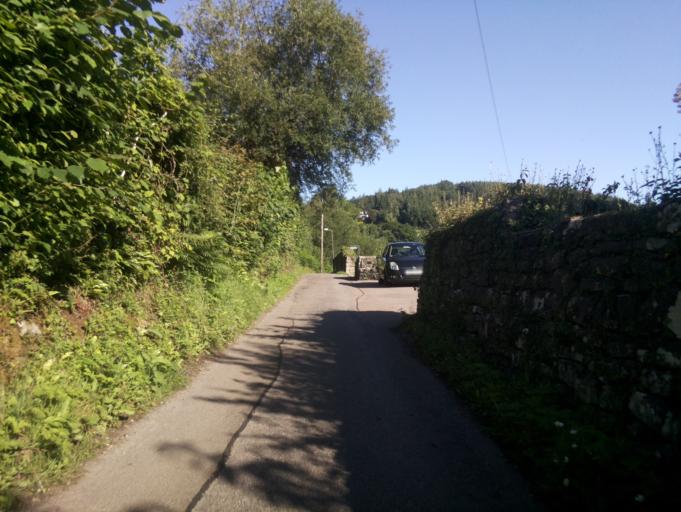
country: GB
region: Wales
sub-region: Monmouthshire
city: Tintern
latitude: 51.6969
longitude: -2.6796
